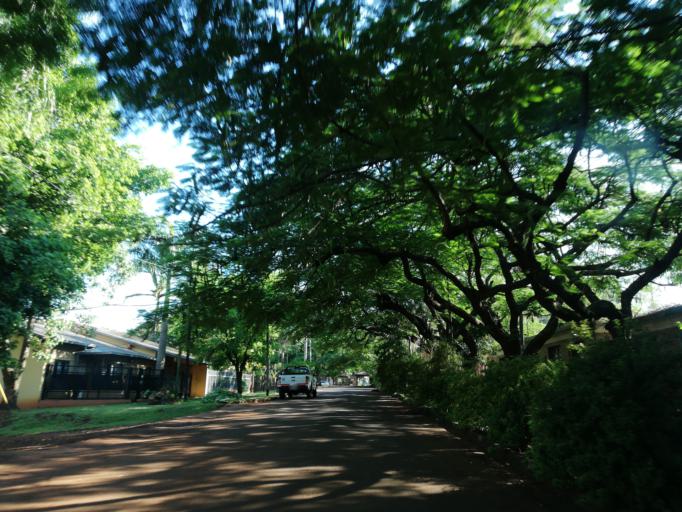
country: AR
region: Misiones
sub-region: Departamento de Capital
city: Posadas
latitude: -27.4023
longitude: -55.9251
